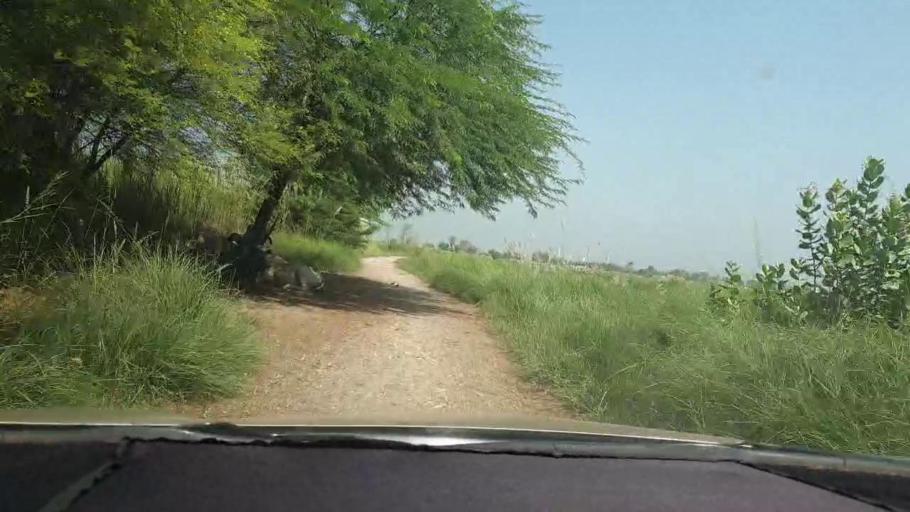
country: PK
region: Sindh
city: Kambar
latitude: 27.6018
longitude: 68.0637
